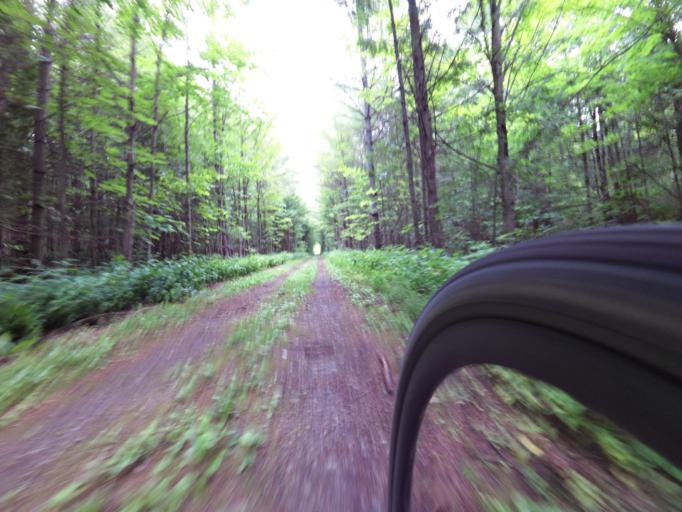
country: CA
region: Ontario
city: Gananoque
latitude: 44.5920
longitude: -76.3046
